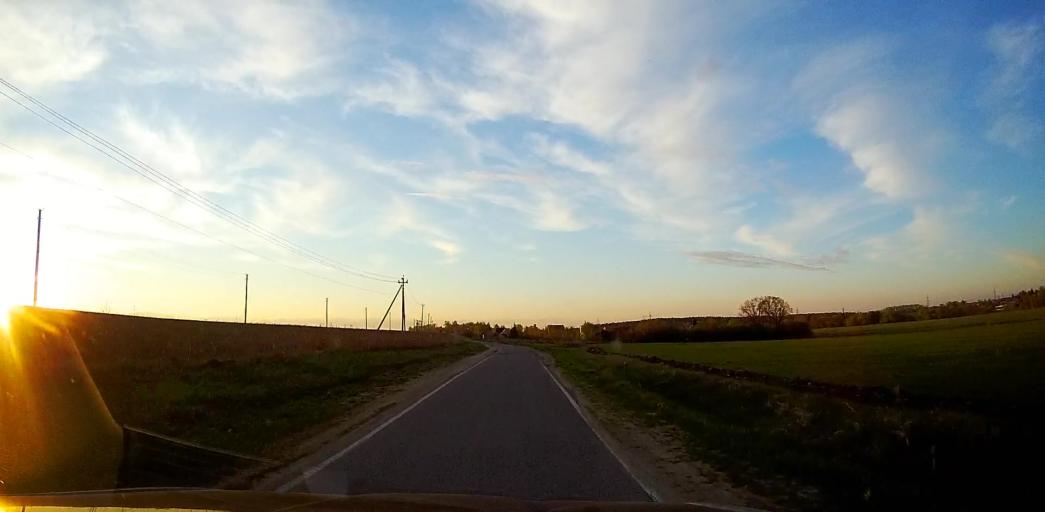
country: RU
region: Moskovskaya
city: Peski
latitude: 55.2240
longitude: 38.7360
